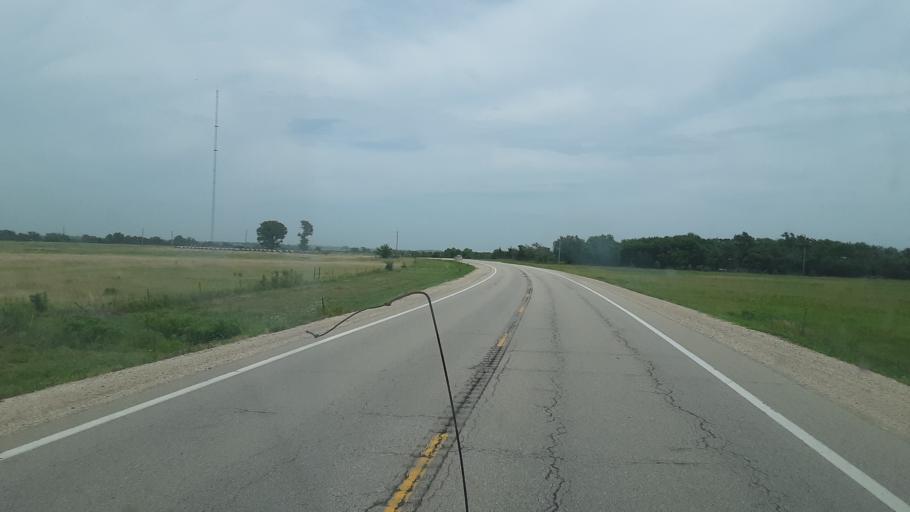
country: US
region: Kansas
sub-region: Woodson County
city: Yates Center
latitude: 37.8369
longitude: -95.8510
